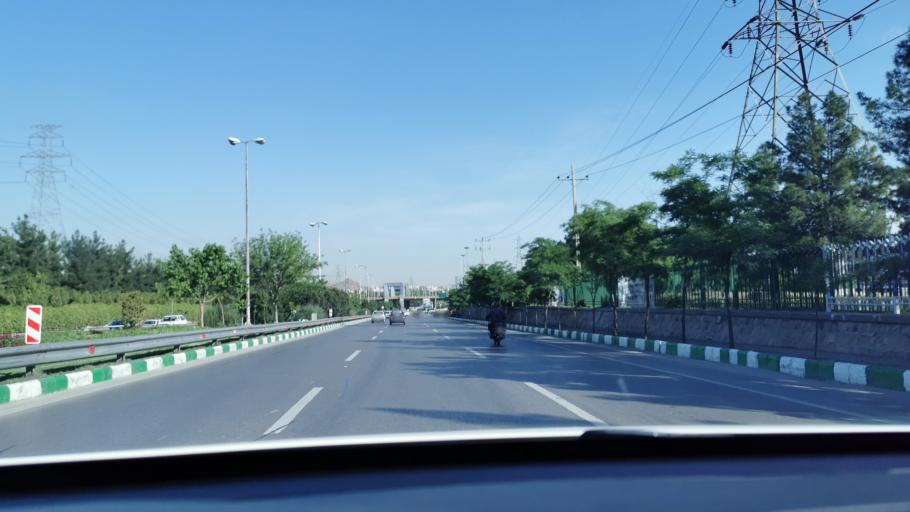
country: IR
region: Razavi Khorasan
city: Mashhad
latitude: 36.2601
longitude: 59.5864
